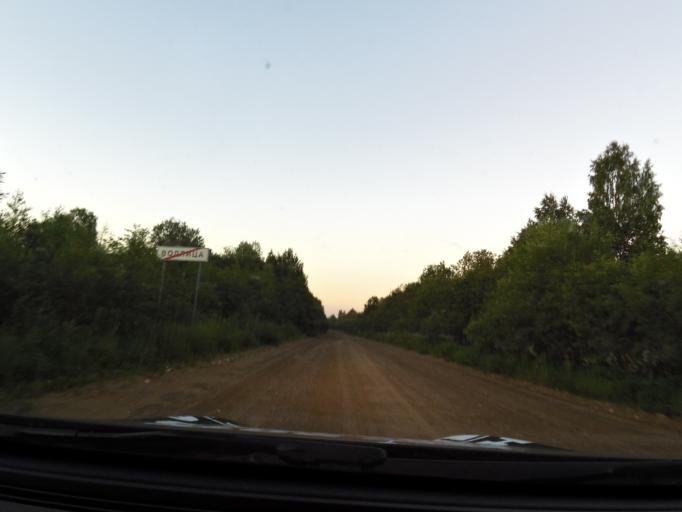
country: RU
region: Leningrad
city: Voznesen'ye
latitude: 60.8387
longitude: 35.7756
